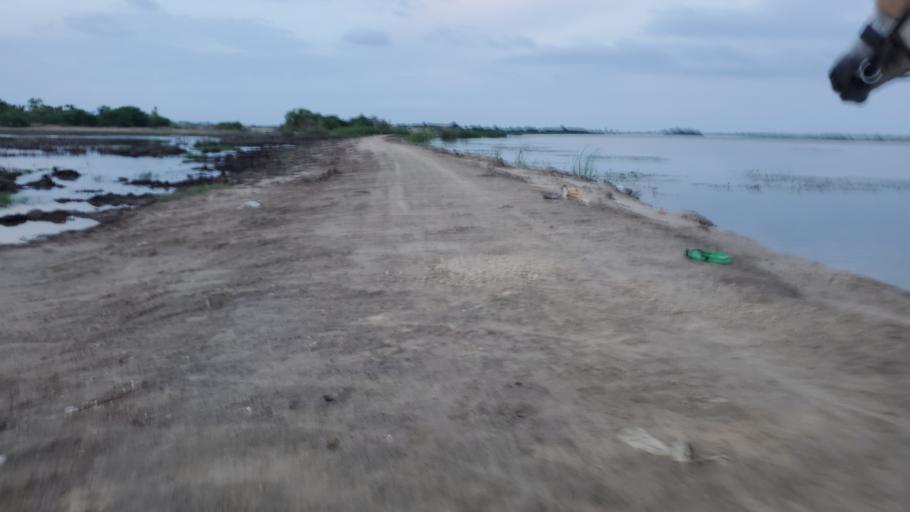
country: SN
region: Saint-Louis
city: Saint-Louis
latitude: 16.0413
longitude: -16.4168
